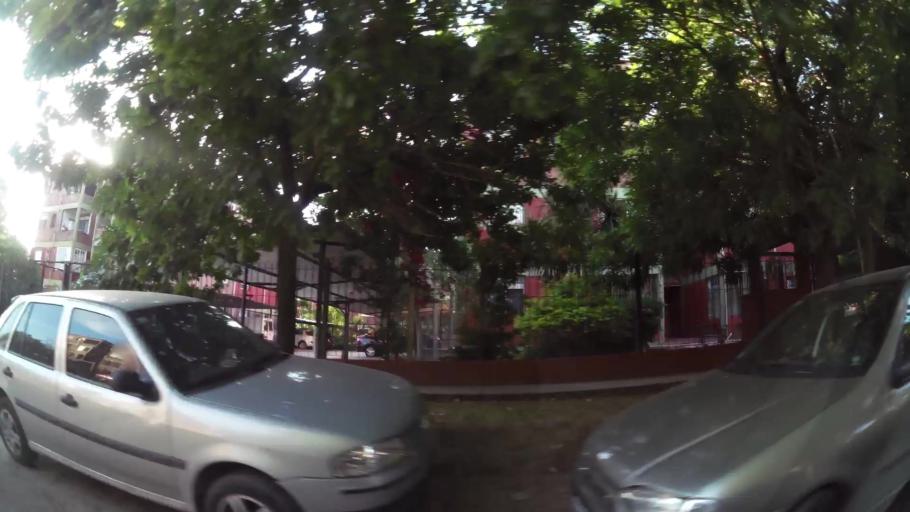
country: AR
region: Buenos Aires F.D.
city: Villa Lugano
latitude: -34.6999
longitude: -58.4909
